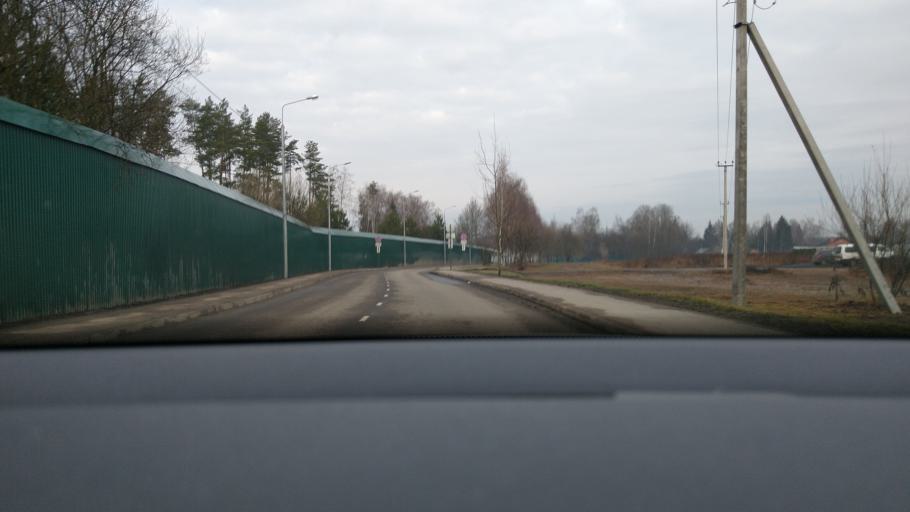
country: RU
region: Moskovskaya
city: Vatutinki
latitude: 55.5147
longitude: 37.3402
